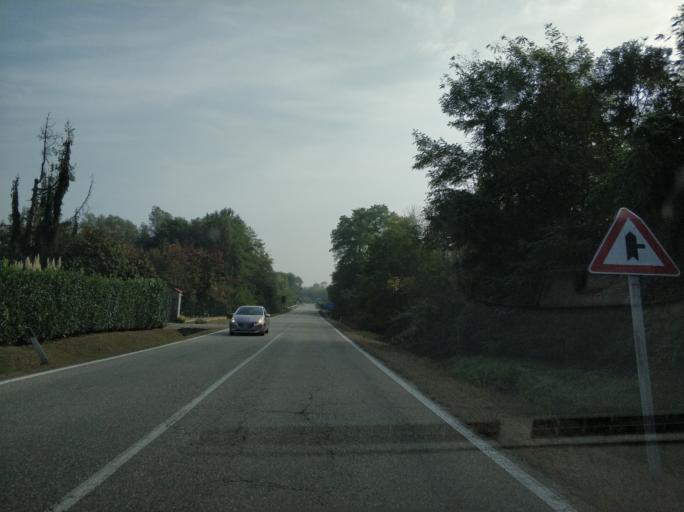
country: IT
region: Piedmont
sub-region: Provincia di Biella
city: Ceresane-Curanuova
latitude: 45.5130
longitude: 7.9978
